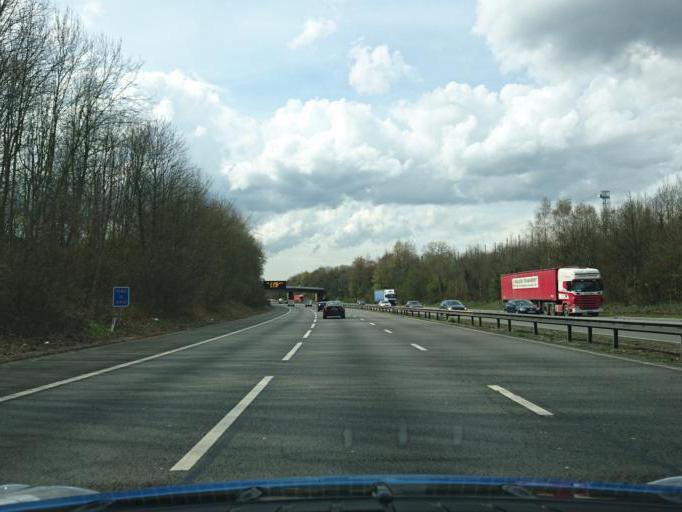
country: GB
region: England
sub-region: Buckinghamshire
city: High Wycombe
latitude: 51.6132
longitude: -0.7433
